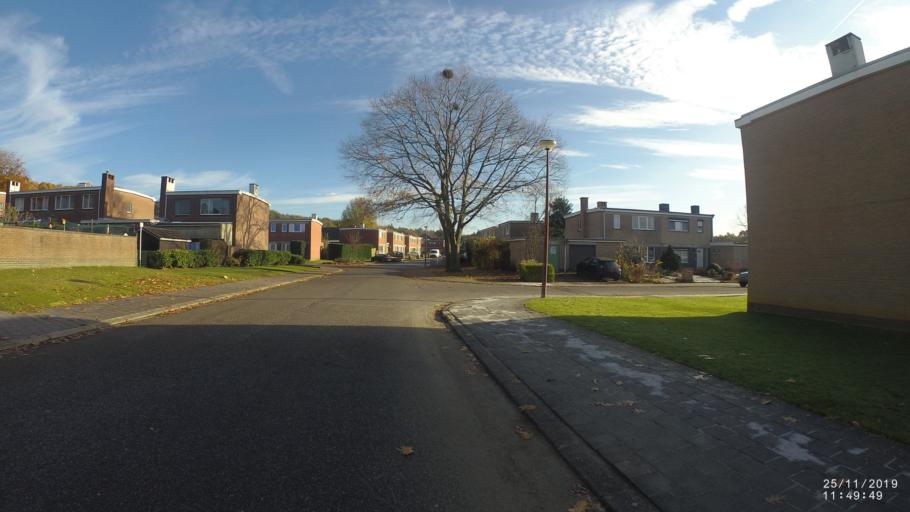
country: BE
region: Flanders
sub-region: Provincie Vlaams-Brabant
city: Aarschot
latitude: 51.0036
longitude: 4.8450
